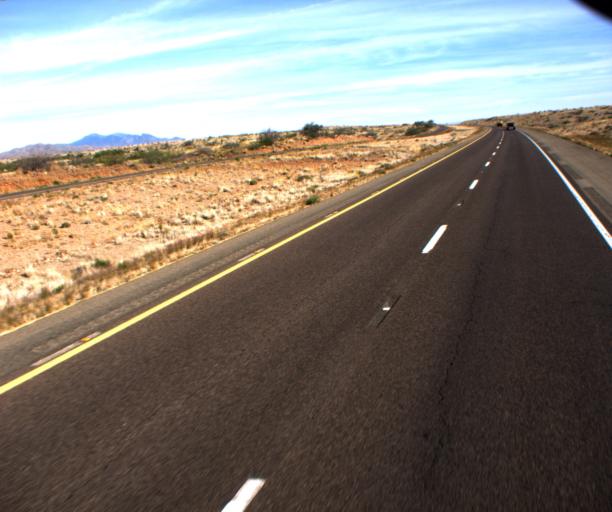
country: US
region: Arizona
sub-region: Cochise County
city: Willcox
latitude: 32.4016
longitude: -109.6619
